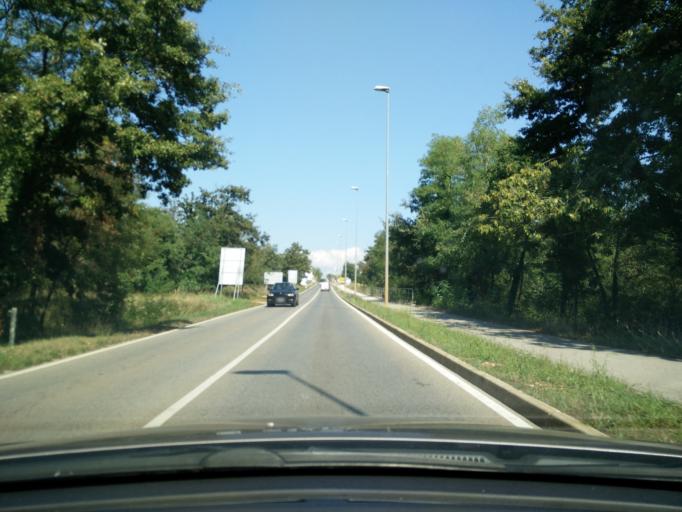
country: HR
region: Istarska
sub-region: Grad Porec
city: Porec
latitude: 45.2572
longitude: 13.6267
